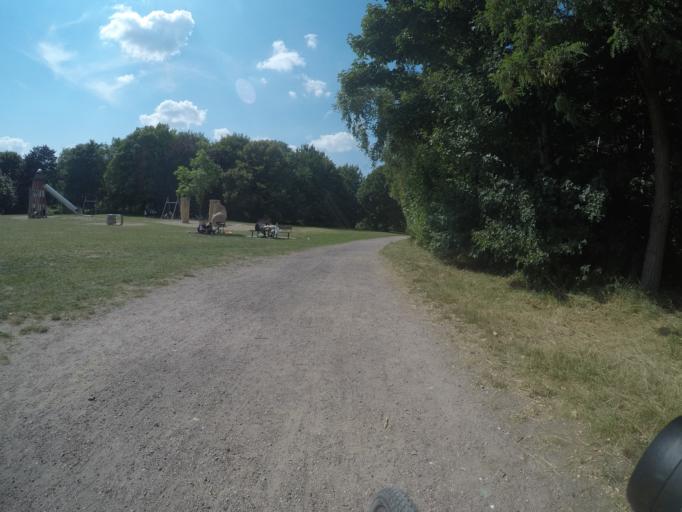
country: DE
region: Schleswig-Holstein
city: Barsbuettel
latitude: 53.5604
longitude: 10.1469
